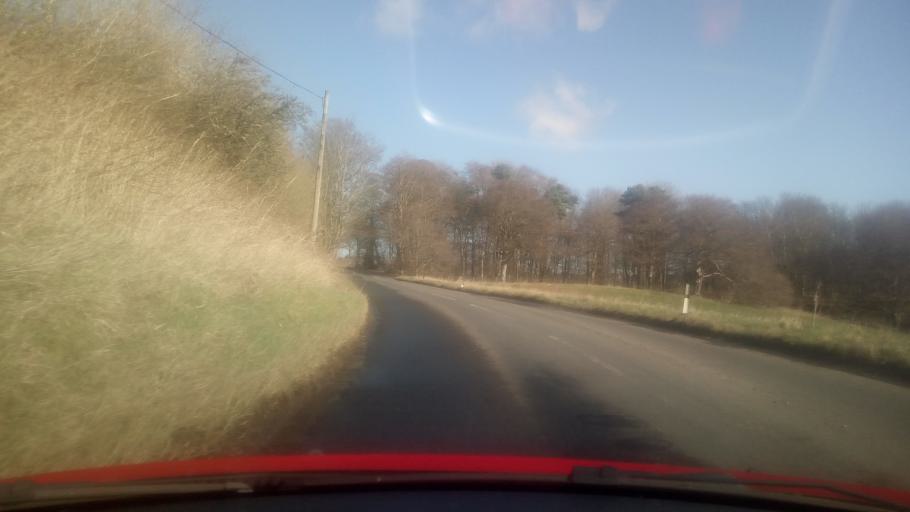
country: GB
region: Scotland
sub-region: The Scottish Borders
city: Selkirk
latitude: 55.5616
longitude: -2.8374
